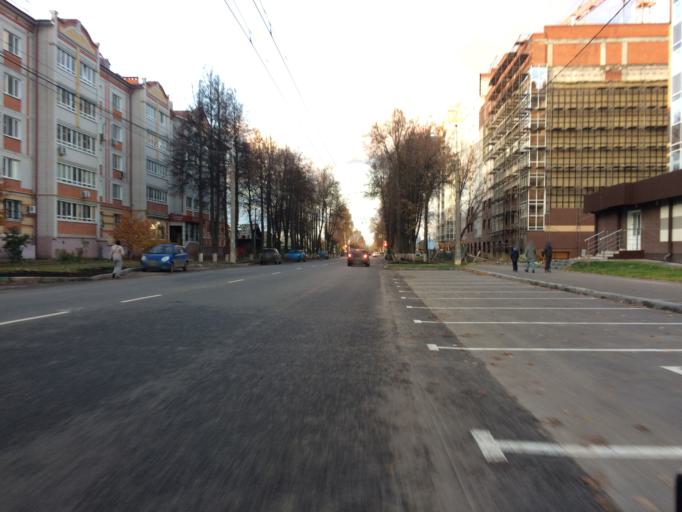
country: RU
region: Mariy-El
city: Yoshkar-Ola
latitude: 56.6485
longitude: 47.8940
